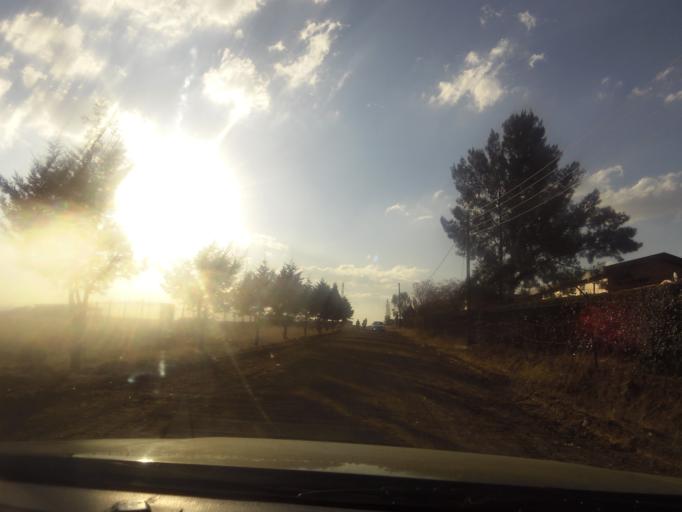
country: LS
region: Berea
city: Teyateyaneng
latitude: -29.1687
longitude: 27.6396
